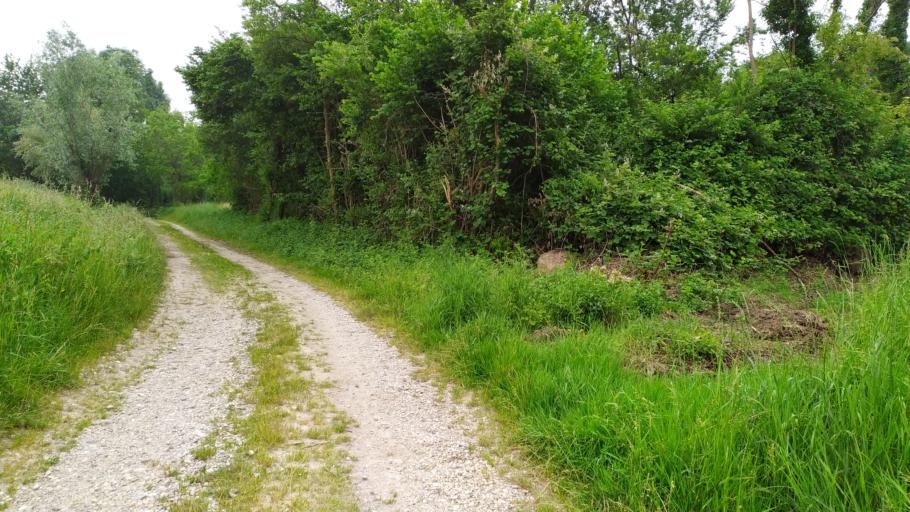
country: IT
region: Friuli Venezia Giulia
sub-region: Provincia di Udine
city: Majano
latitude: 46.1914
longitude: 13.0407
